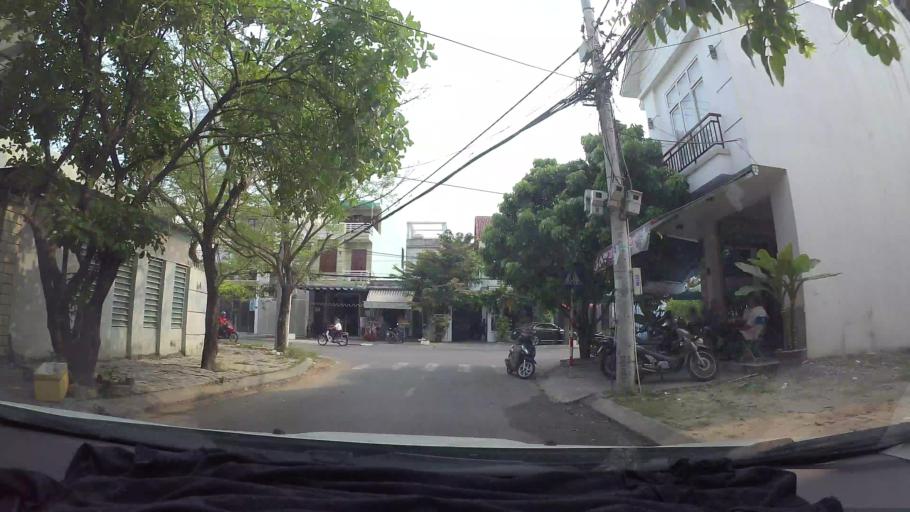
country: VN
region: Da Nang
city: Cam Le
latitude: 16.0409
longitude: 108.2141
